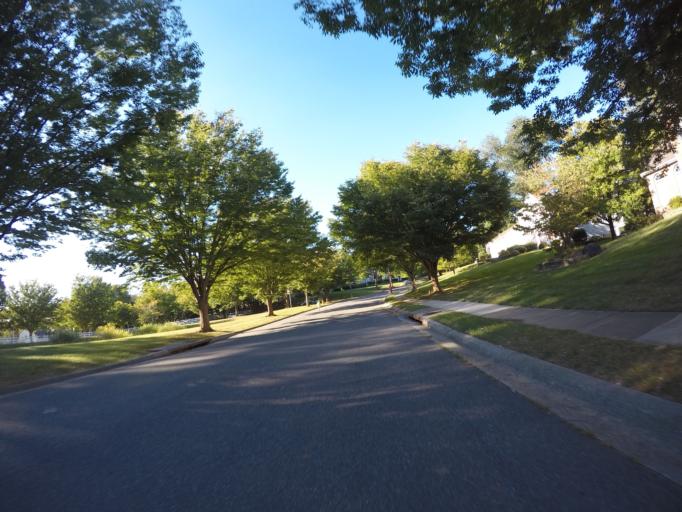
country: US
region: Maryland
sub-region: Howard County
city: Ellicott City
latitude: 39.2940
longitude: -76.8094
